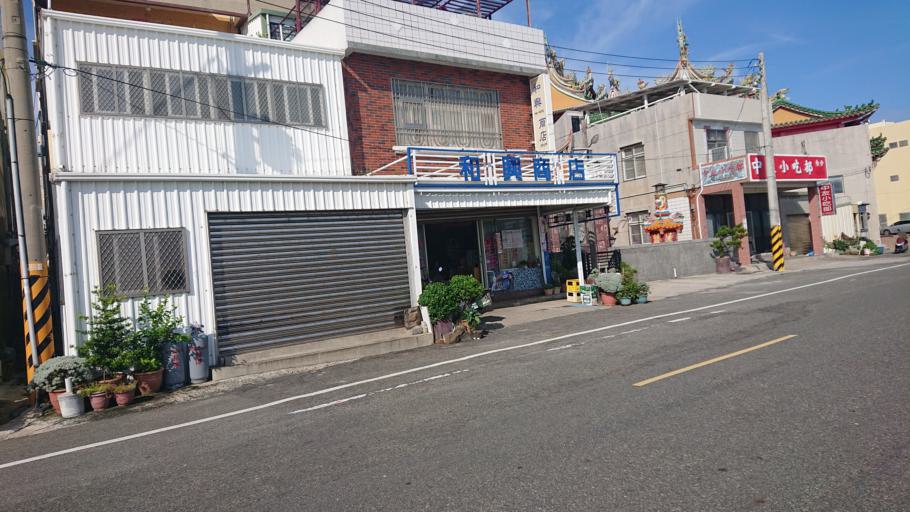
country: TW
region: Taiwan
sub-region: Penghu
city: Ma-kung
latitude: 23.5249
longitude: 119.5697
